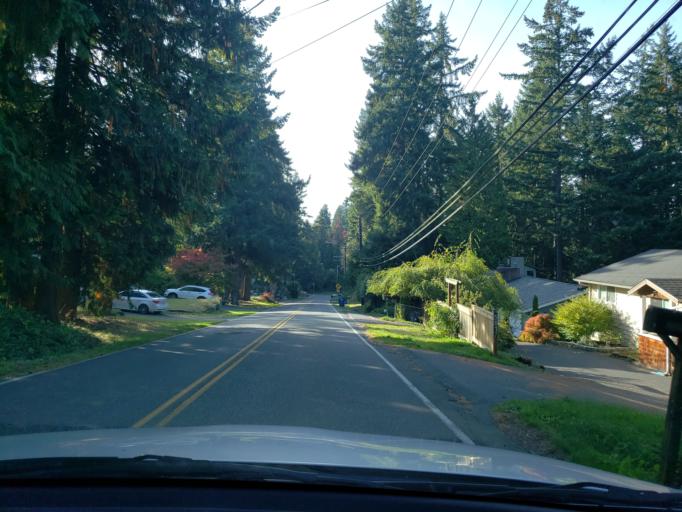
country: US
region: Washington
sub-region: Snohomish County
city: Meadowdale
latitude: 47.8644
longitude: -122.3123
